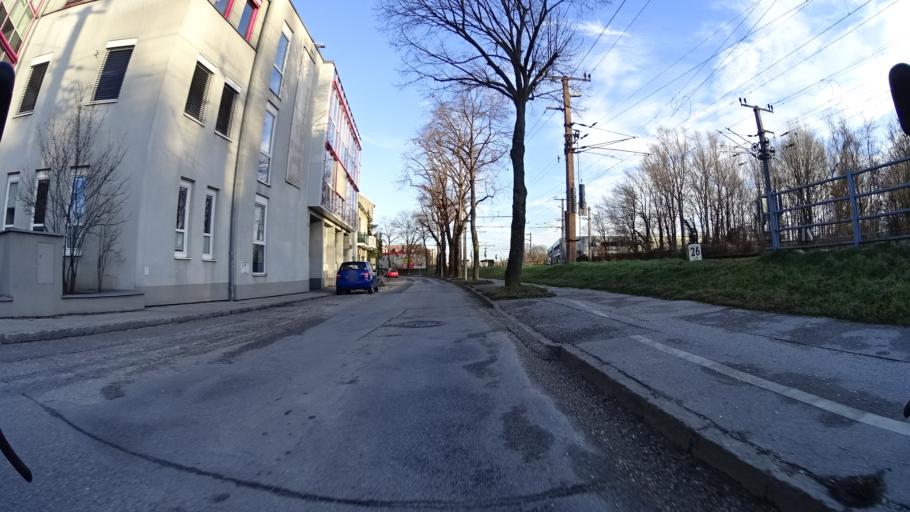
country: AT
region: Lower Austria
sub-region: Politischer Bezirk Korneuburg
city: Stockerau
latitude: 48.3829
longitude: 16.2097
